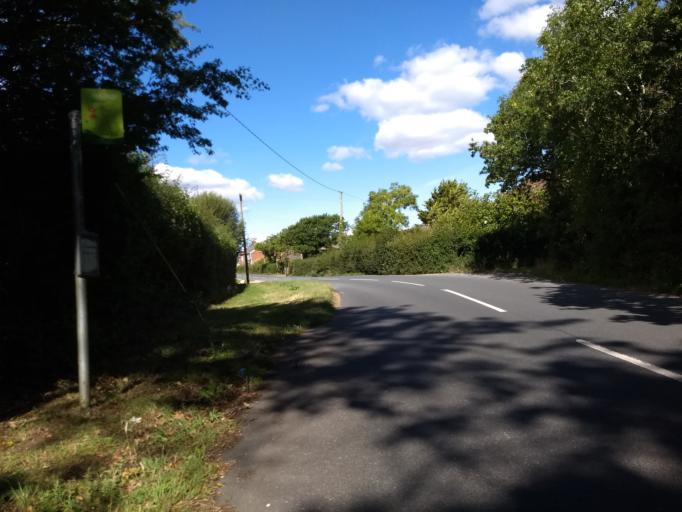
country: GB
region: England
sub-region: Isle of Wight
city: Ryde
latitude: 50.7117
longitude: -1.1859
